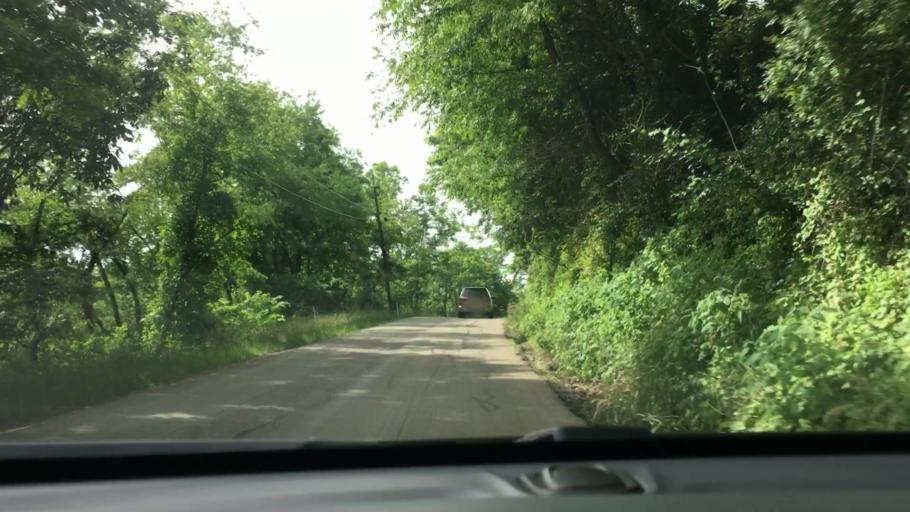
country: US
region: Pennsylvania
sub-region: Westmoreland County
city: New Stanton
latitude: 40.2553
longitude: -79.6108
